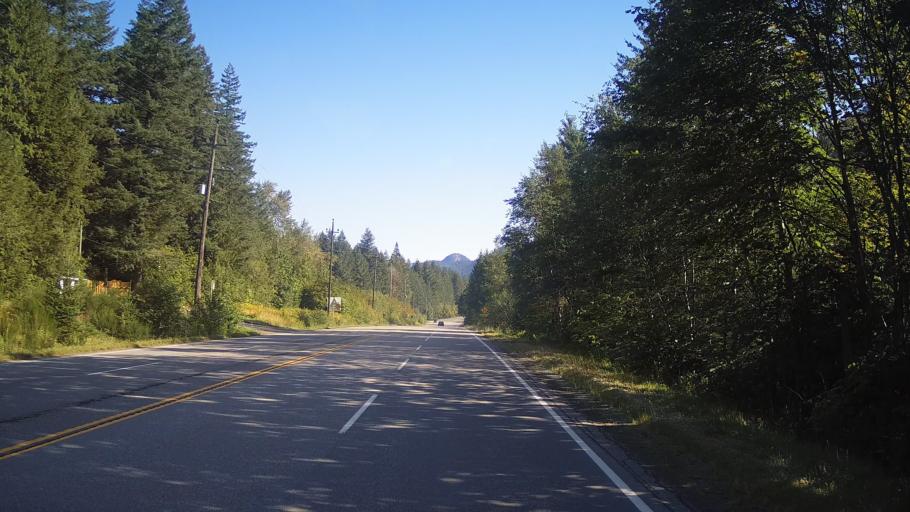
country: CA
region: British Columbia
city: Hope
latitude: 49.4973
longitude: -121.4202
